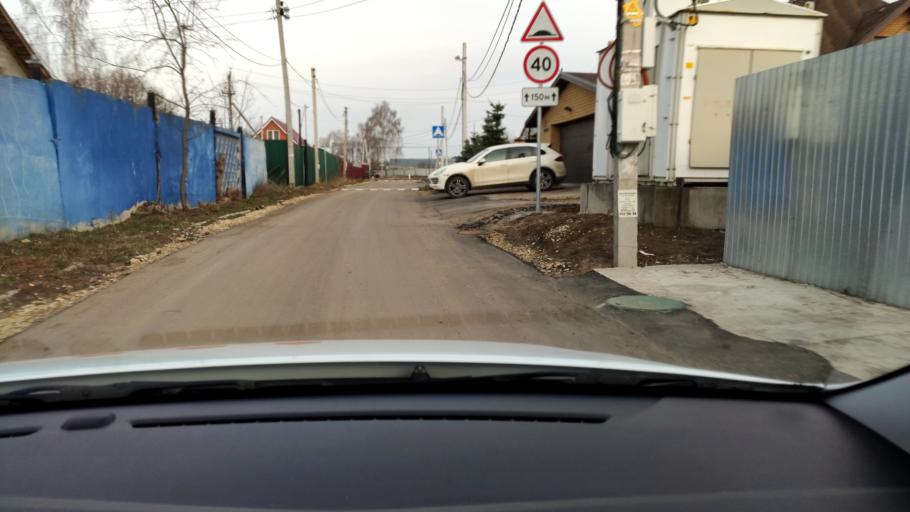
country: RU
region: Tatarstan
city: Stolbishchi
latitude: 55.7410
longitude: 49.2676
